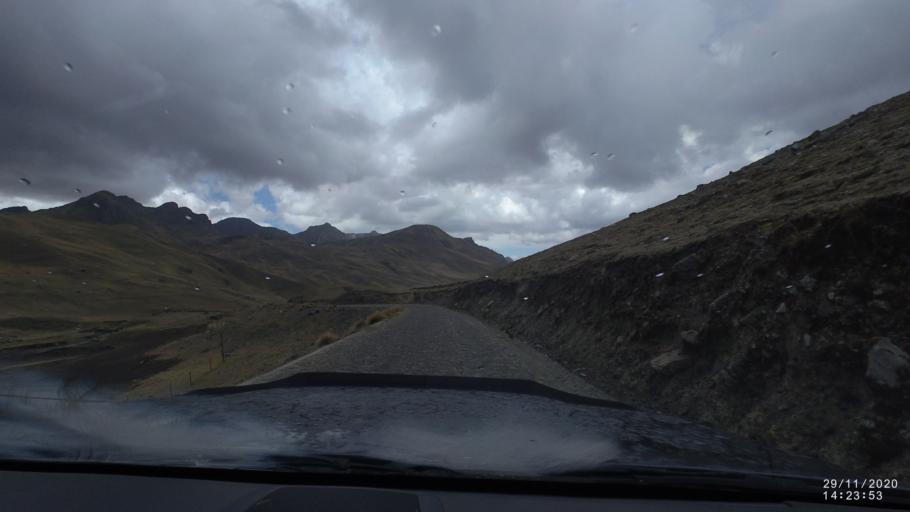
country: BO
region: Cochabamba
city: Sipe Sipe
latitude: -17.2548
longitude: -66.3819
